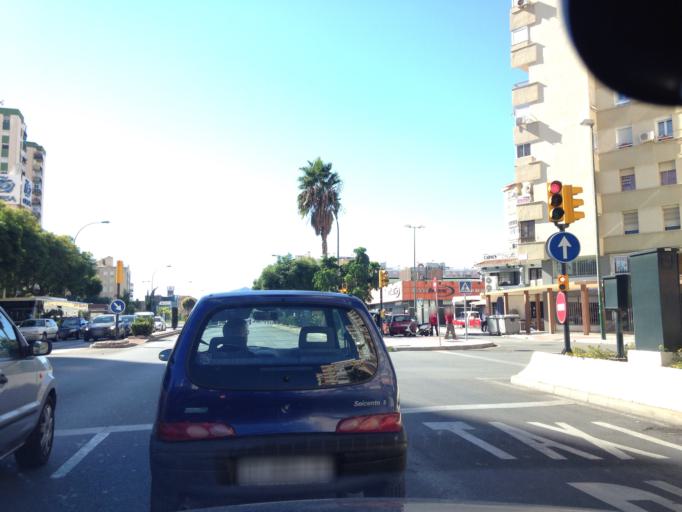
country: ES
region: Andalusia
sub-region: Provincia de Malaga
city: Malaga
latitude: 36.6933
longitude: -4.4540
